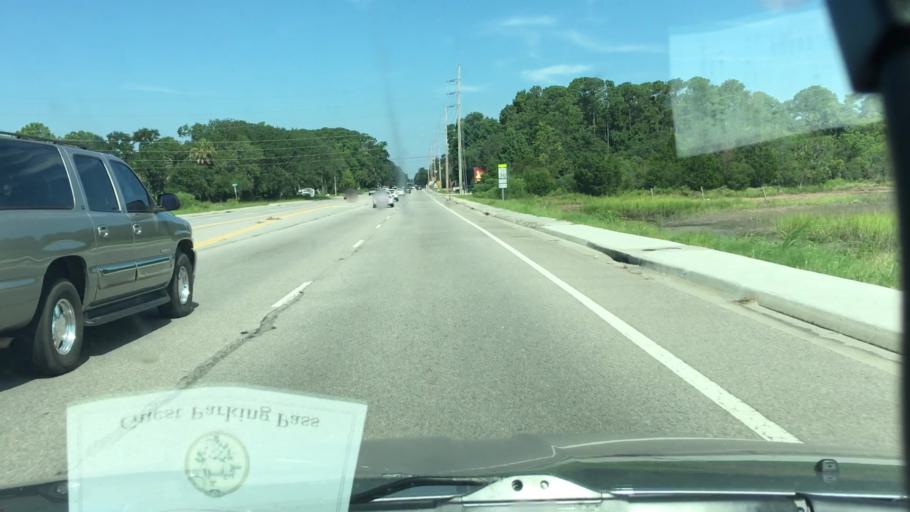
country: US
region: South Carolina
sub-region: Beaufort County
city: Beaufort
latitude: 32.4100
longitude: -80.6424
